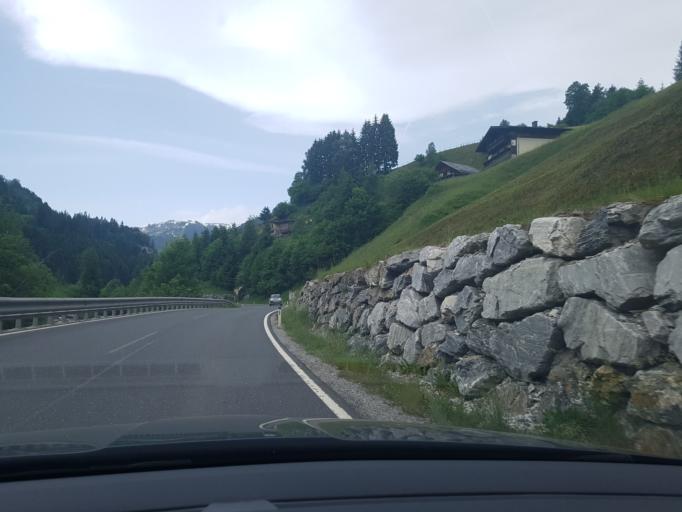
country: AT
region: Salzburg
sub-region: Politischer Bezirk Sankt Johann im Pongau
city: Schwarzach im Pongau
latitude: 47.2726
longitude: 13.2114
